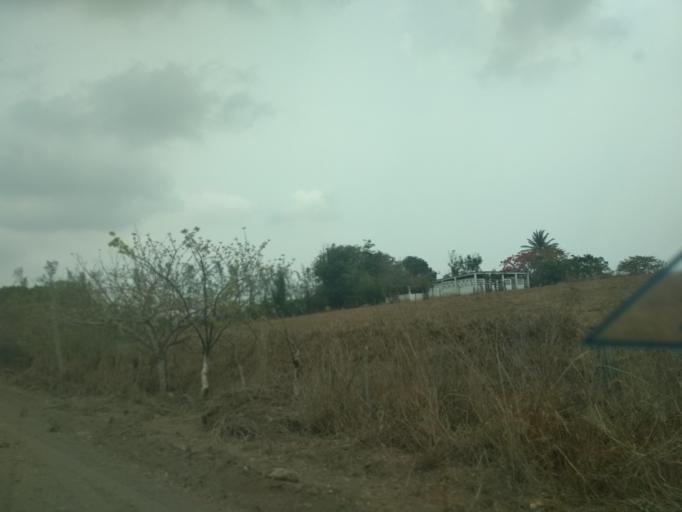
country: MX
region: Veracruz
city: Paso del Toro
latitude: 19.0158
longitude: -96.1344
